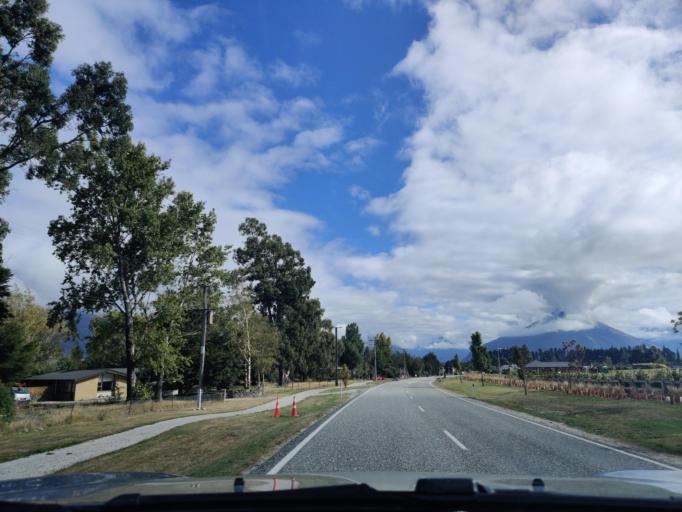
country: NZ
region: Otago
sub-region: Queenstown-Lakes District
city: Queenstown
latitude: -44.8564
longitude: 168.3912
